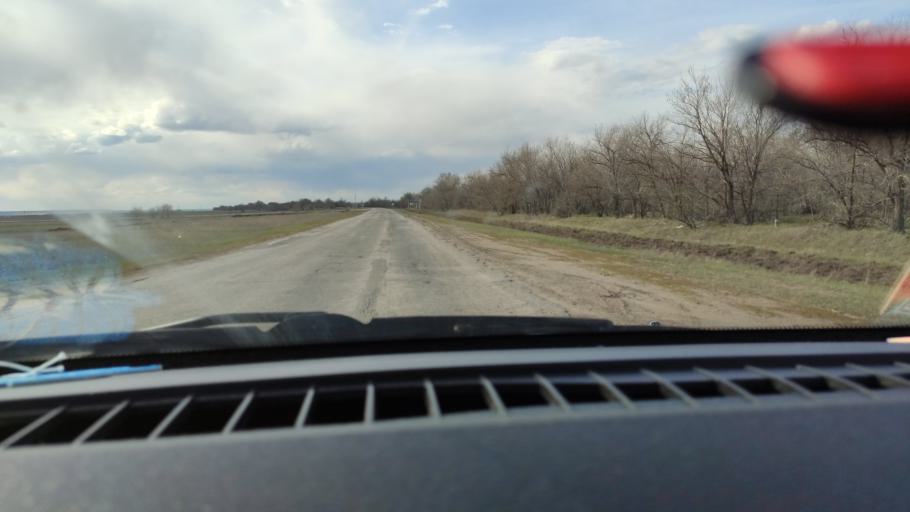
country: RU
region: Saratov
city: Rovnoye
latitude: 51.0377
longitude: 46.0766
